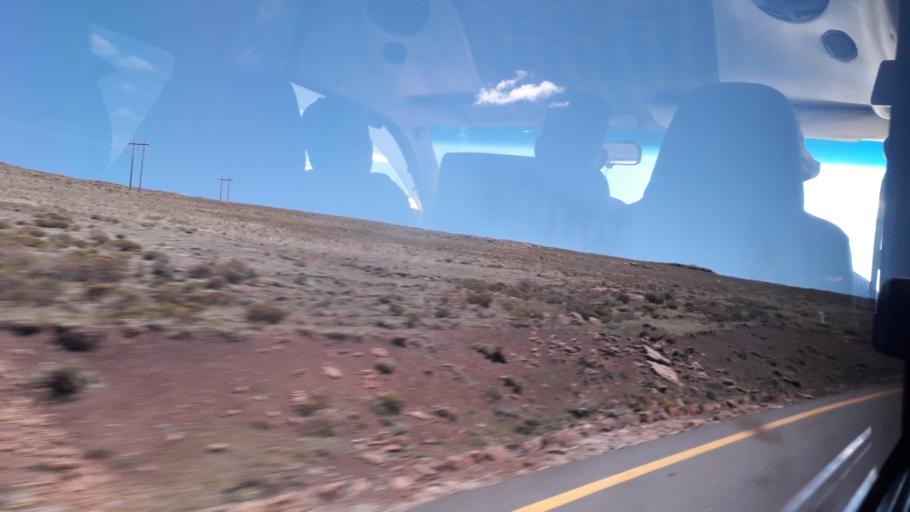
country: LS
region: Mokhotlong
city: Mokhotlong
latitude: -29.0614
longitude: 28.8504
